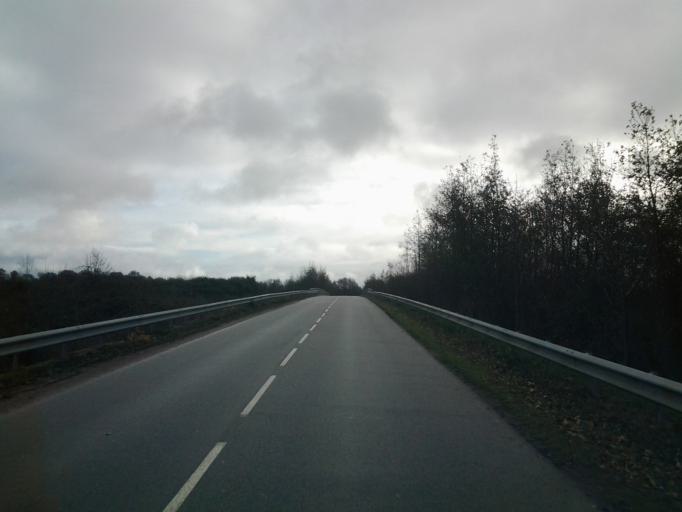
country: FR
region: Pays de la Loire
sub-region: Departement de la Vendee
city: La Roche-sur-Yon
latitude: 46.6536
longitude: -1.3861
